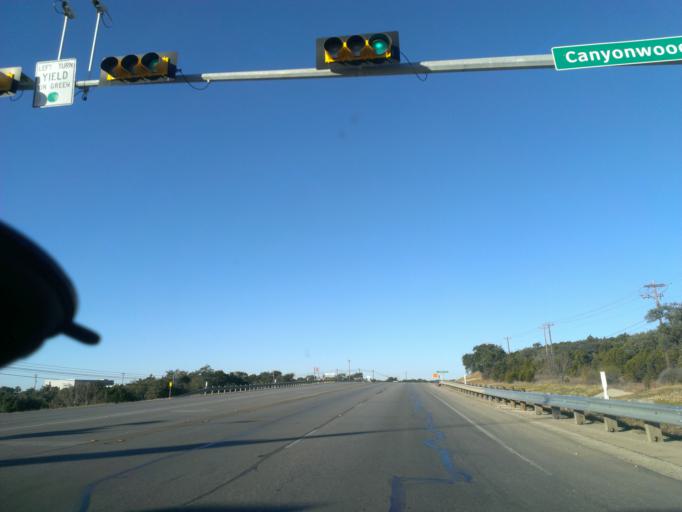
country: US
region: Texas
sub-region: Hays County
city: Dripping Springs
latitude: 30.1950
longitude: -98.0298
